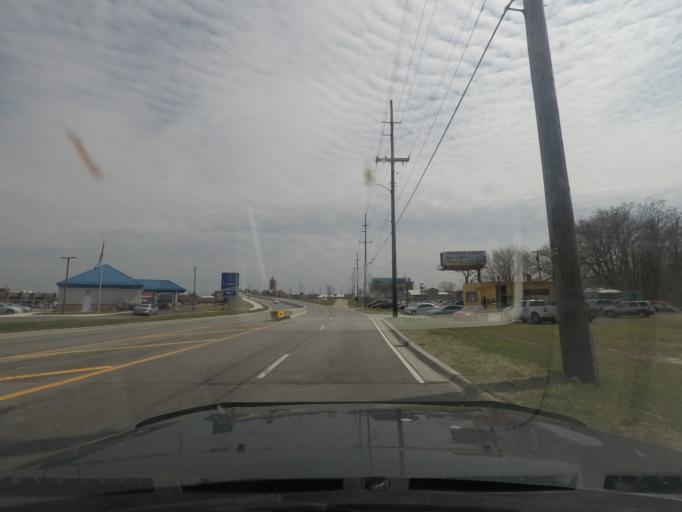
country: US
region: Indiana
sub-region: LaPorte County
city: LaPorte
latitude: 41.6143
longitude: -86.7294
